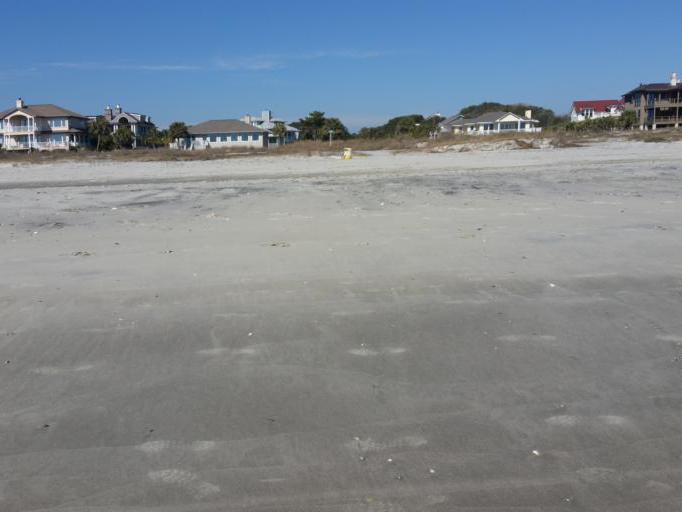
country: US
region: South Carolina
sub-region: Charleston County
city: Isle of Palms
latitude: 32.7966
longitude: -79.7555
